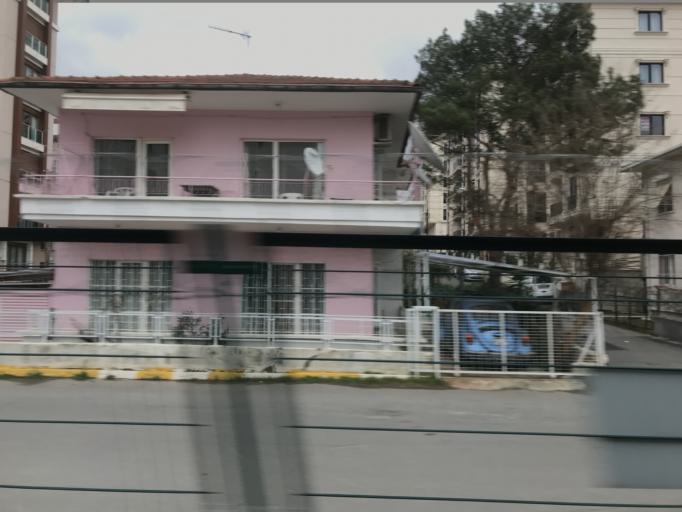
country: TR
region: Istanbul
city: Pendik
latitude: 40.8778
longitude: 29.2419
